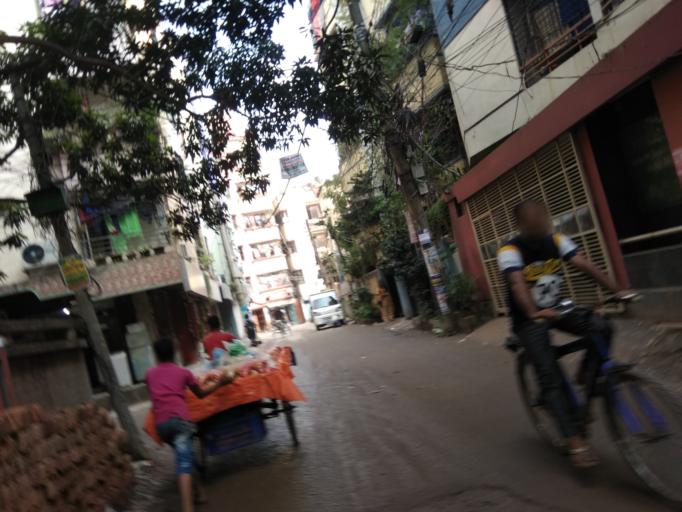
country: BD
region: Dhaka
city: Azimpur
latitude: 23.7645
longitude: 90.3543
